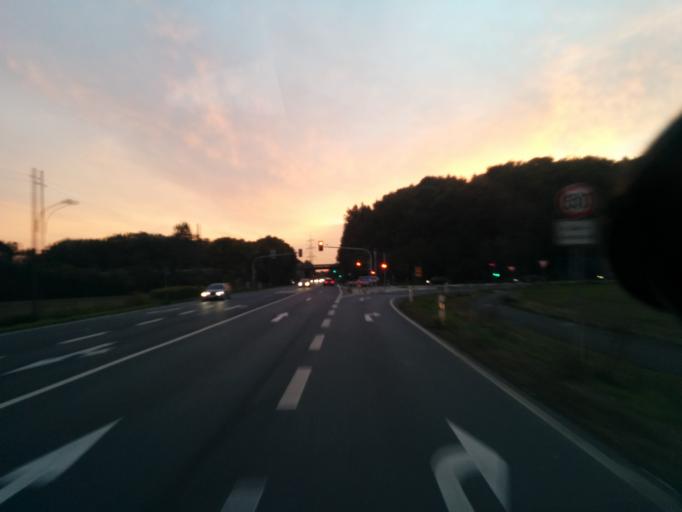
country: DE
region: North Rhine-Westphalia
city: Witten
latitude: 51.4615
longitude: 7.3871
